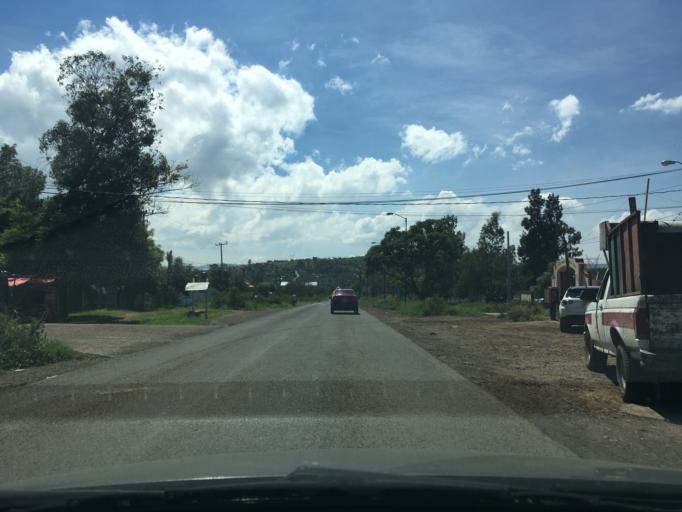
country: MX
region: Michoacan
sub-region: Morelia
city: San Antonio
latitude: 19.6782
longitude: -101.2791
